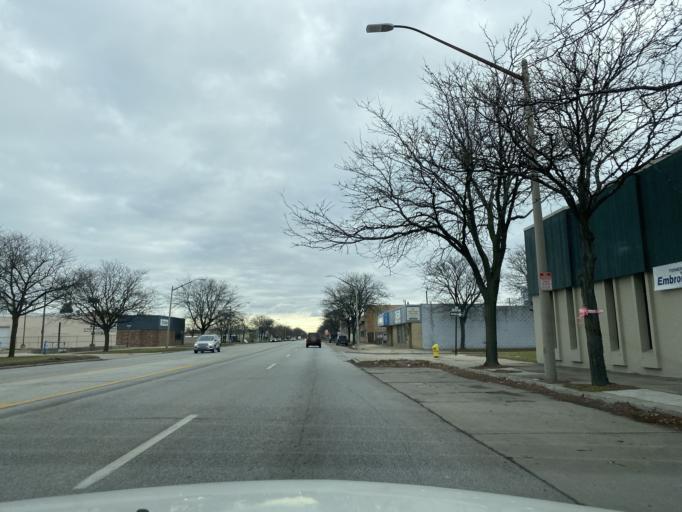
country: US
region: Michigan
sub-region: Wayne County
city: Southgate
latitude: 42.1994
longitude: -83.1784
